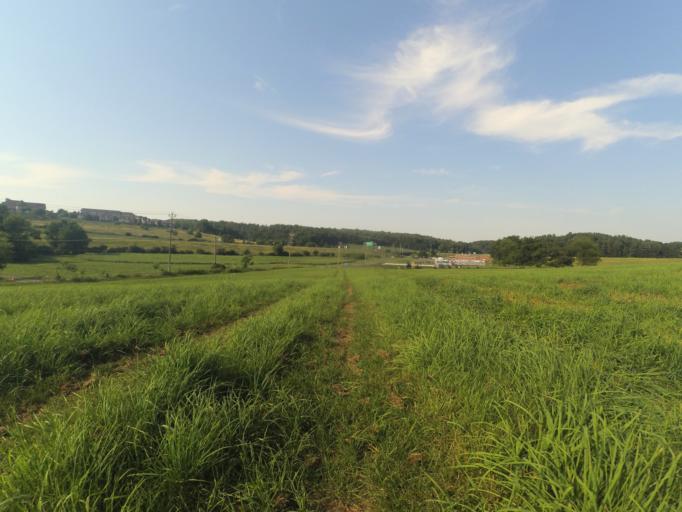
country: US
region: Pennsylvania
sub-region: Centre County
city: State College
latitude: 40.8196
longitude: -77.8705
